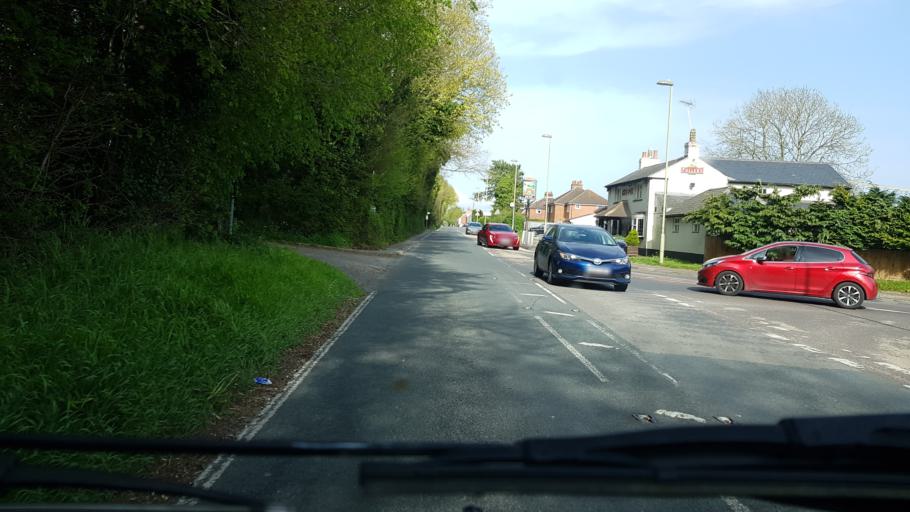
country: GB
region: England
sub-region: Hampshire
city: Basingstoke
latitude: 51.2584
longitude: -1.1685
